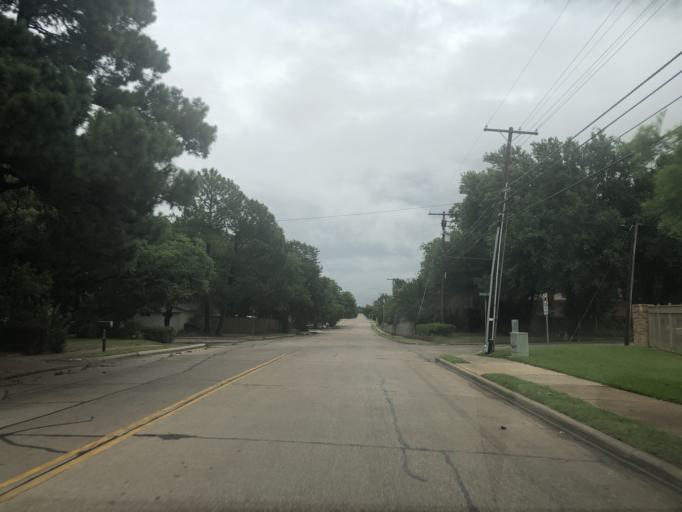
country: US
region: Texas
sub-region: Dallas County
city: Irving
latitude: 32.7939
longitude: -96.9437
